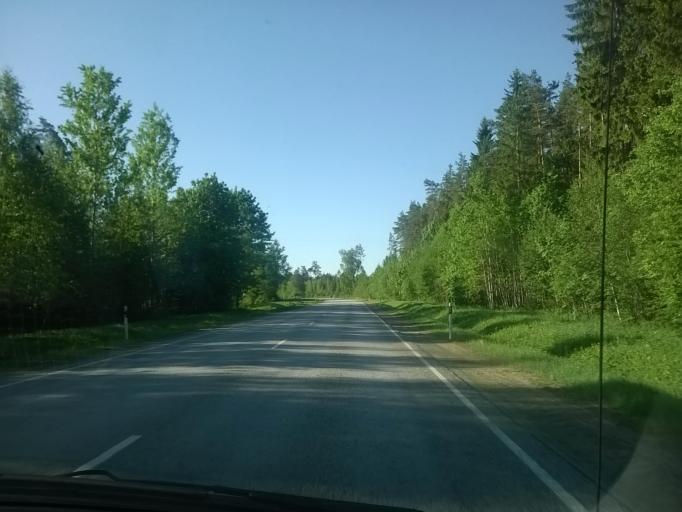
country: EE
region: Valgamaa
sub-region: Valga linn
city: Valga
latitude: 57.9564
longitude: 26.1625
